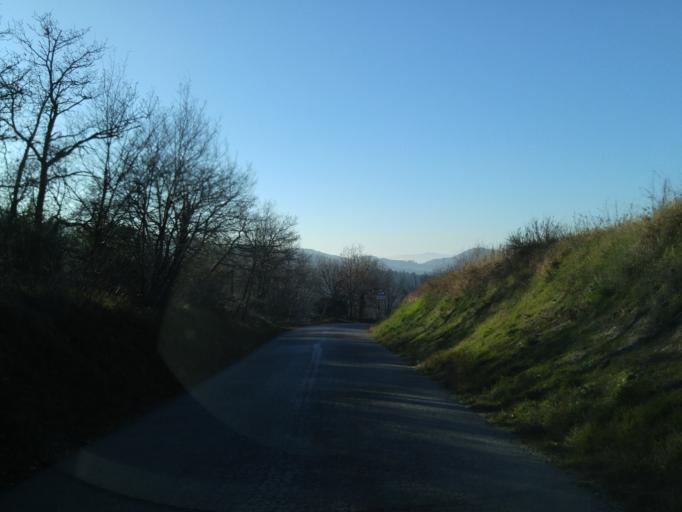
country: IT
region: The Marches
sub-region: Provincia di Pesaro e Urbino
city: Isola del Piano
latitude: 43.7174
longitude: 12.7482
